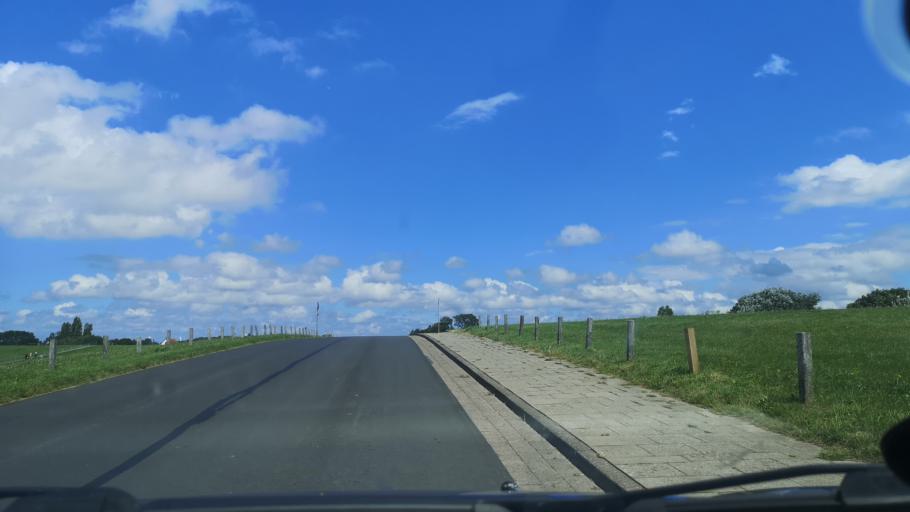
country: DE
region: Lower Saxony
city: Wremen
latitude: 53.6468
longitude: 8.4952
